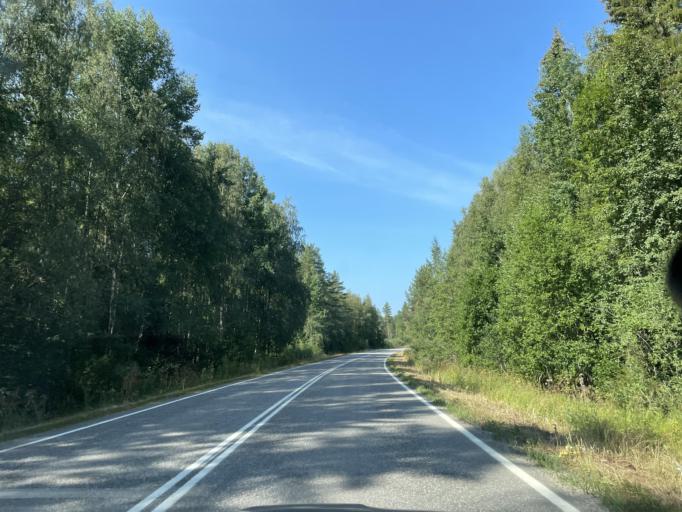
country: FI
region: Central Finland
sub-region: Saarijaervi-Viitasaari
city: Pihtipudas
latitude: 63.3748
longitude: 25.6001
